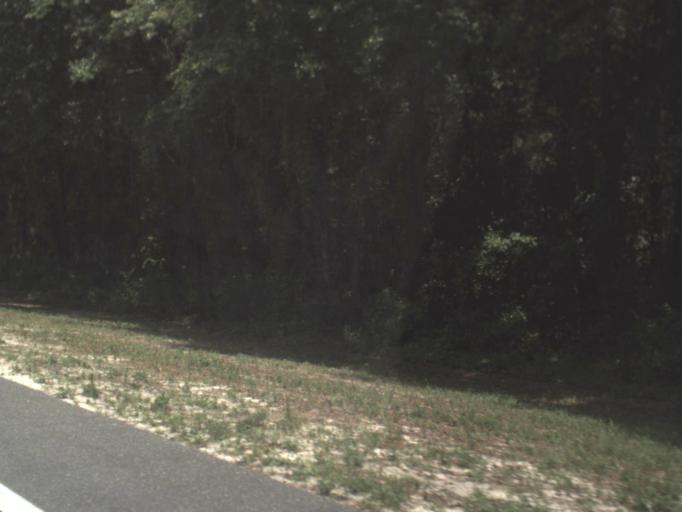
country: US
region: Florida
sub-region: Levy County
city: Williston
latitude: 29.4238
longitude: -82.4233
